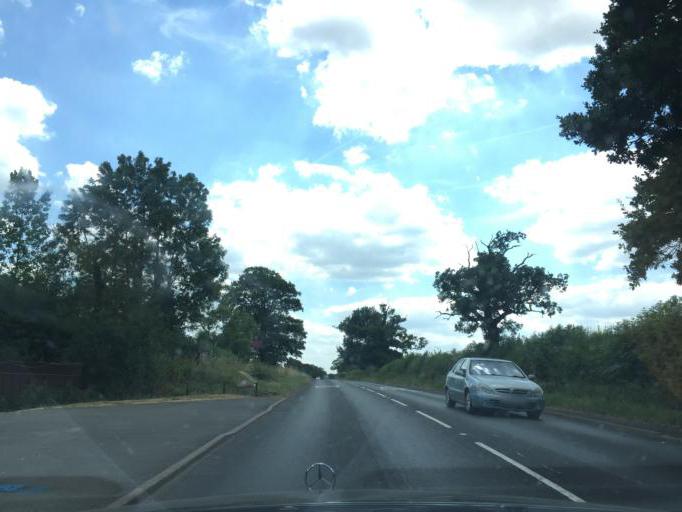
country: GB
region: England
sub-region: Warwickshire
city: Bedworth
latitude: 52.4542
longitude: -1.4086
